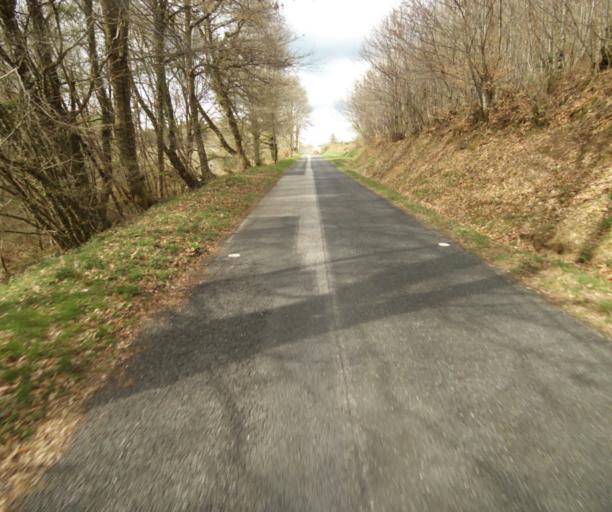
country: FR
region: Limousin
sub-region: Departement de la Correze
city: Argentat
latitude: 45.2079
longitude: 1.9662
